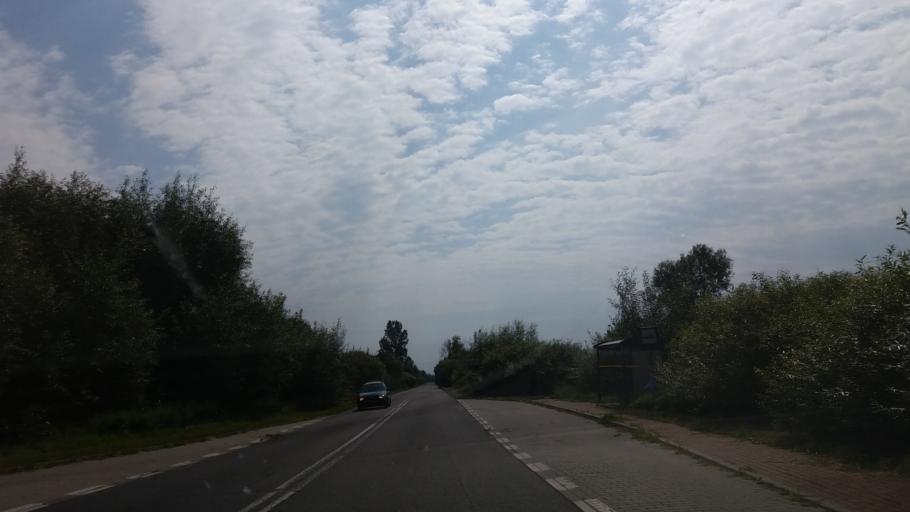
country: PL
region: Lubusz
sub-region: Powiat strzelecko-drezdenecki
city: Stare Kurowo
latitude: 52.8093
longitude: 15.6373
